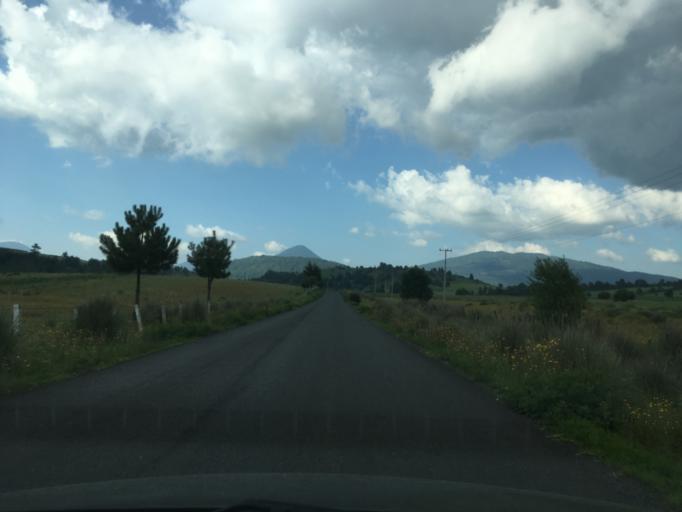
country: MX
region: Michoacan
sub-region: Nahuatzen
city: Sevina
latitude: 19.6087
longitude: -101.9391
